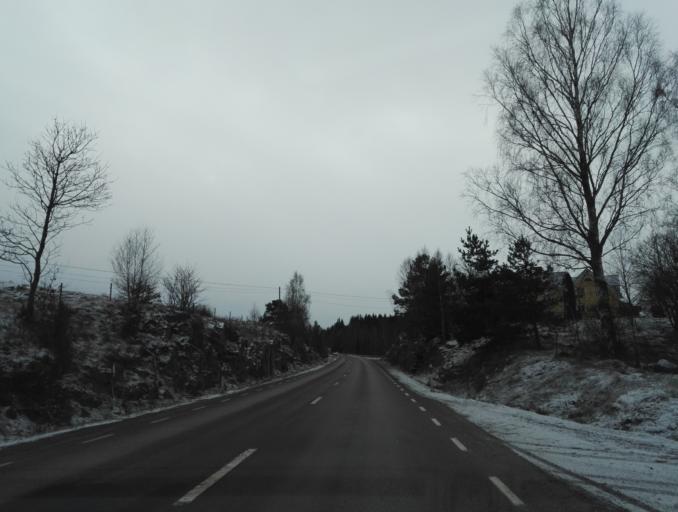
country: SE
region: Kalmar
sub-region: Hultsfreds Kommun
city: Virserum
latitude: 57.2861
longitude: 15.5658
